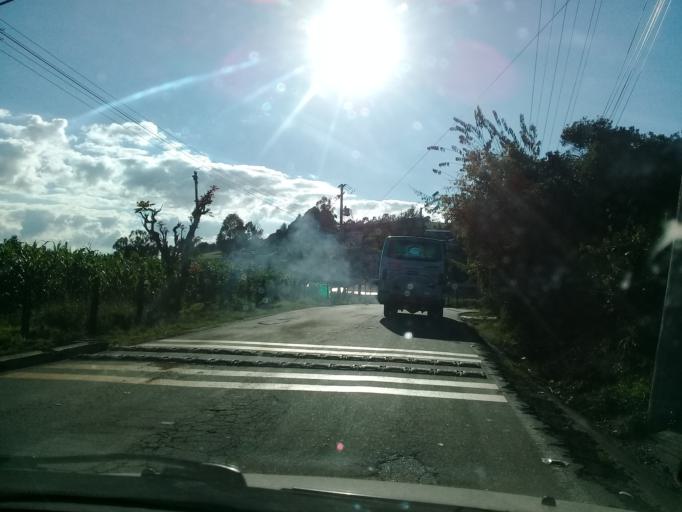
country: CO
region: Cundinamarca
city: Tabio
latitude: 4.8964
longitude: -74.1119
